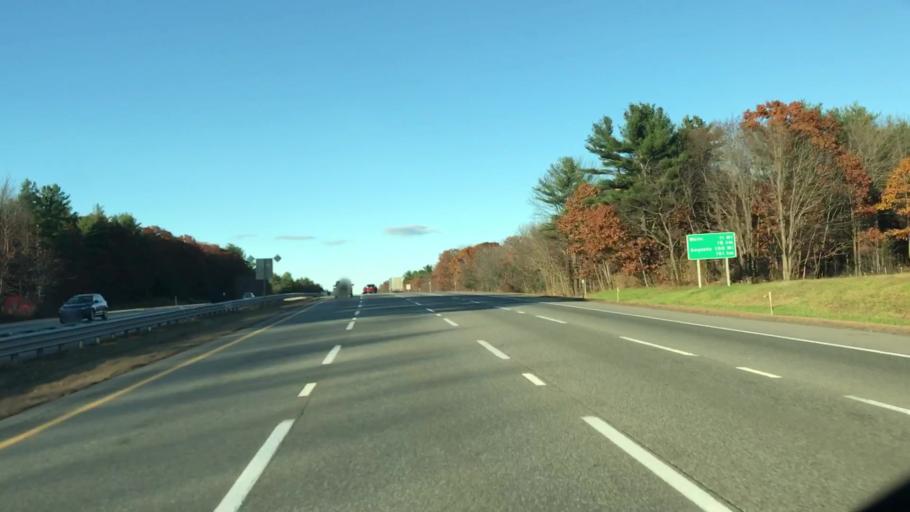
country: US
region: Maine
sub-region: York County
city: York Harbor
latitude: 43.1668
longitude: -70.6535
